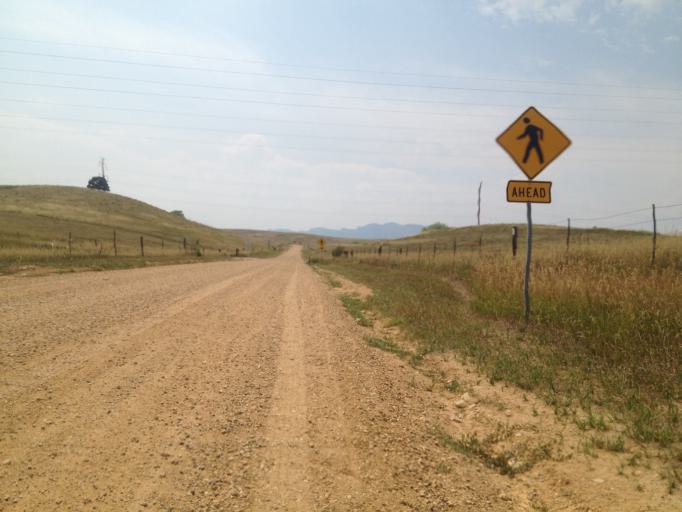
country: US
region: Colorado
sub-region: Boulder County
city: Superior
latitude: 39.9520
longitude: -105.1784
